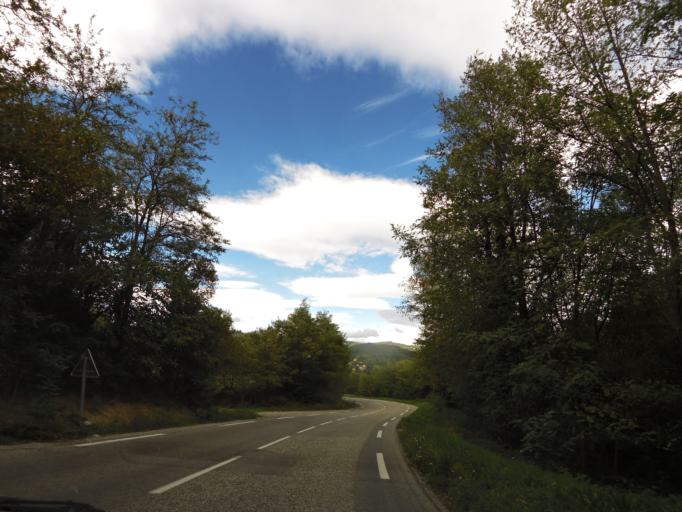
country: FR
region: Languedoc-Roussillon
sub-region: Departement du Gard
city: Lasalle
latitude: 44.0283
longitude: 3.8602
